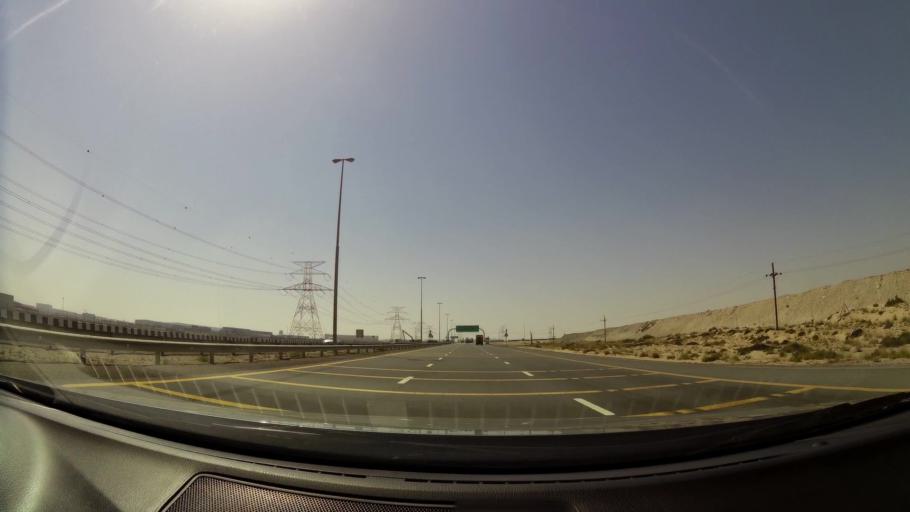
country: AE
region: Dubai
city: Dubai
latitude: 24.9294
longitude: 55.0881
